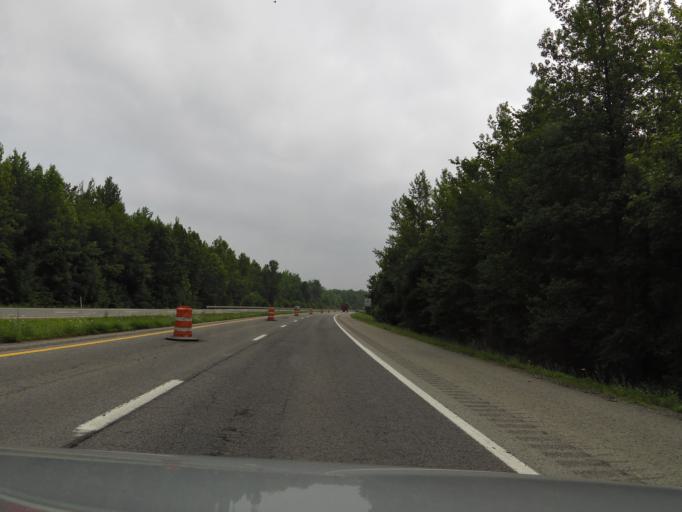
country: US
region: Kentucky
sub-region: Muhlenberg County
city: Morehead
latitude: 37.2691
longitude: -87.1610
